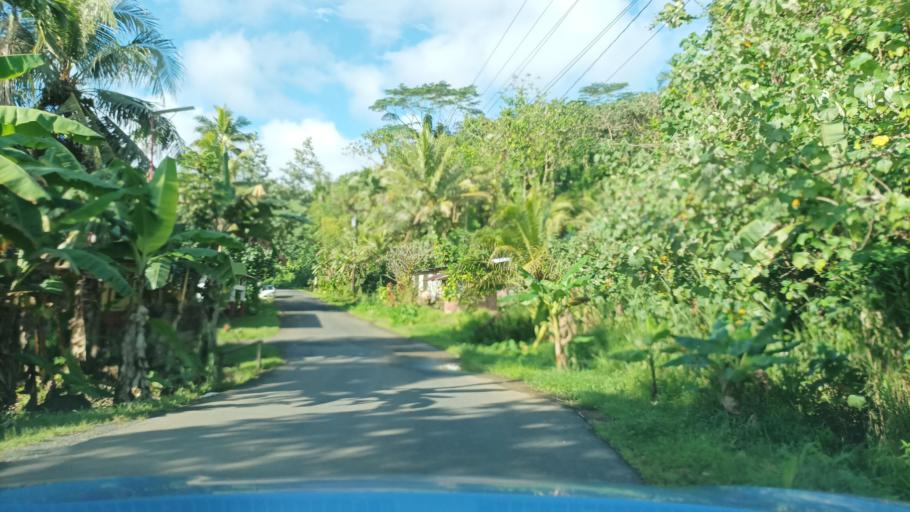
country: FM
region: Pohnpei
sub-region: Kolonia Municipality
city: Kolonia Town
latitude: 6.9589
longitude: 158.1852
